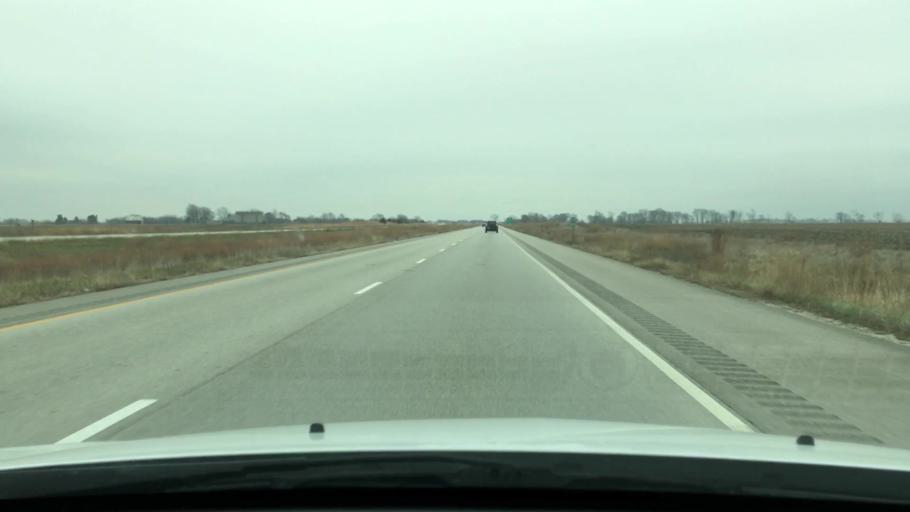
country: US
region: Illinois
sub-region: Morgan County
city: Jacksonville
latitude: 39.7373
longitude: -90.0758
